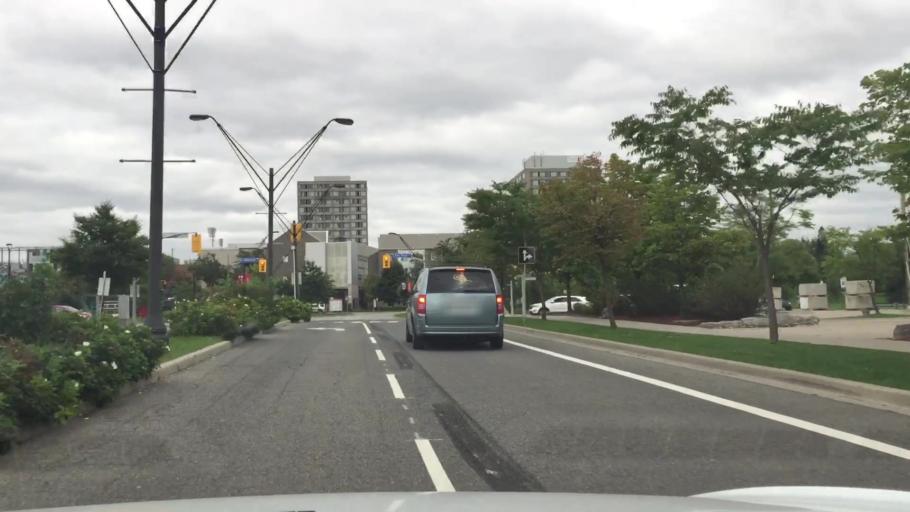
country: CA
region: Ontario
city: Concord
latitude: 43.7723
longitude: -79.5123
